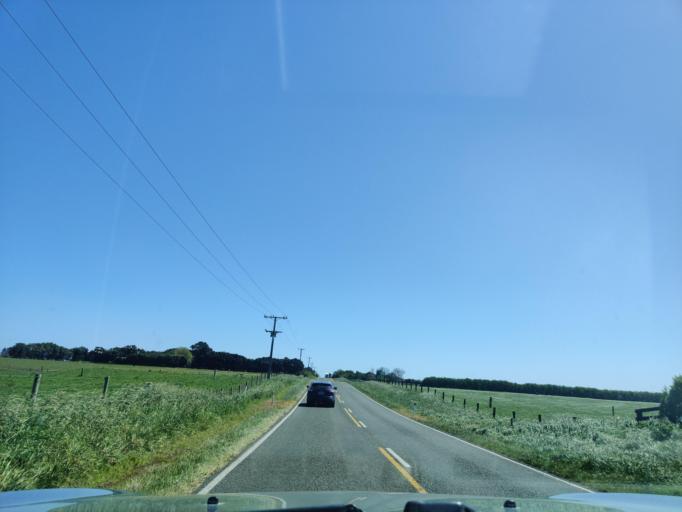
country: NZ
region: Taranaki
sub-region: South Taranaki District
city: Hawera
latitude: -39.5495
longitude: 174.1117
